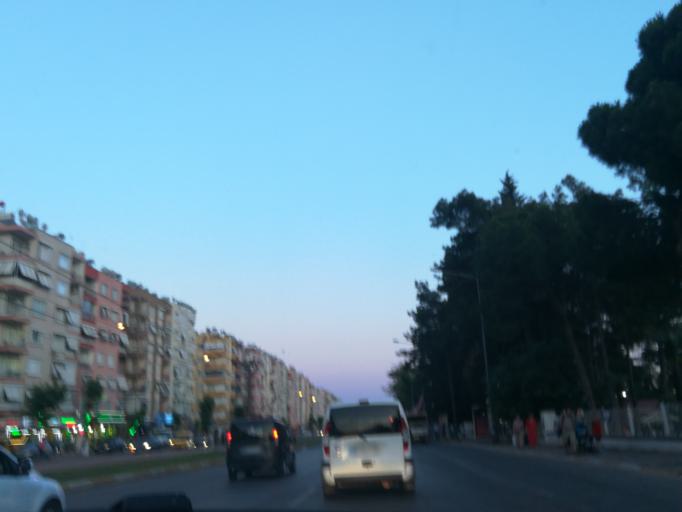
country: TR
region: Antalya
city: Antalya
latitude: 36.9130
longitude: 30.6769
